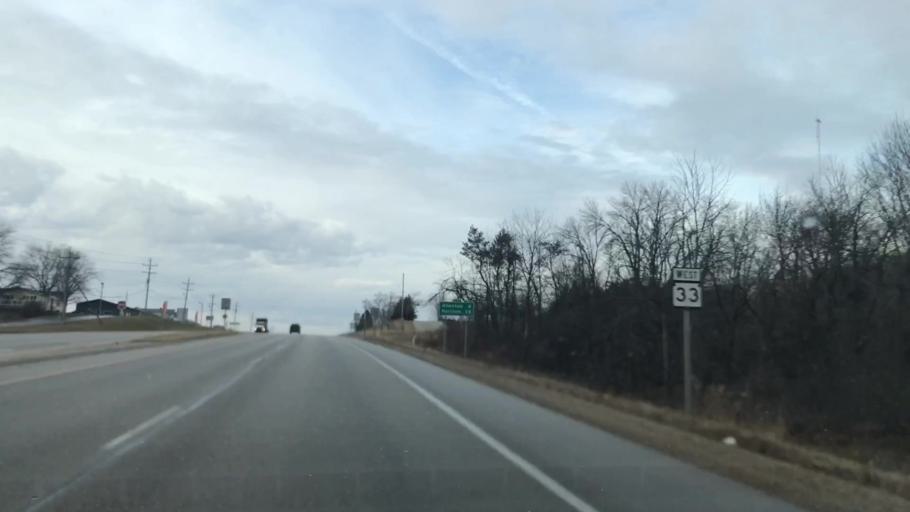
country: US
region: Wisconsin
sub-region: Washington County
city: West Bend
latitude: 43.4276
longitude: -88.2628
